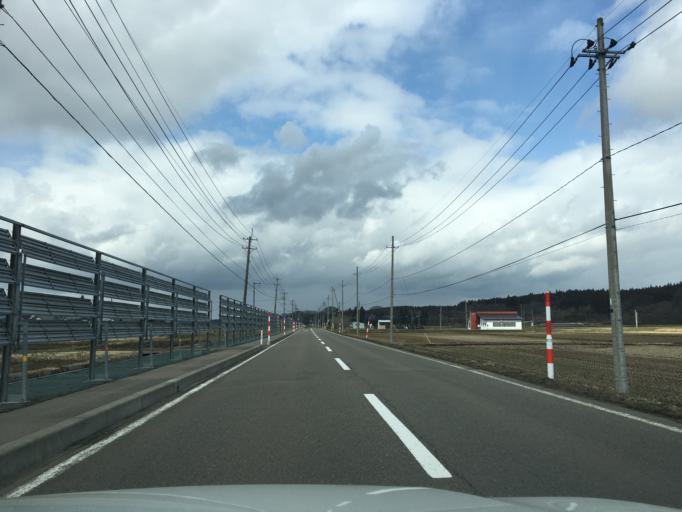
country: JP
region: Akita
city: Takanosu
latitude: 40.1361
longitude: 140.3542
